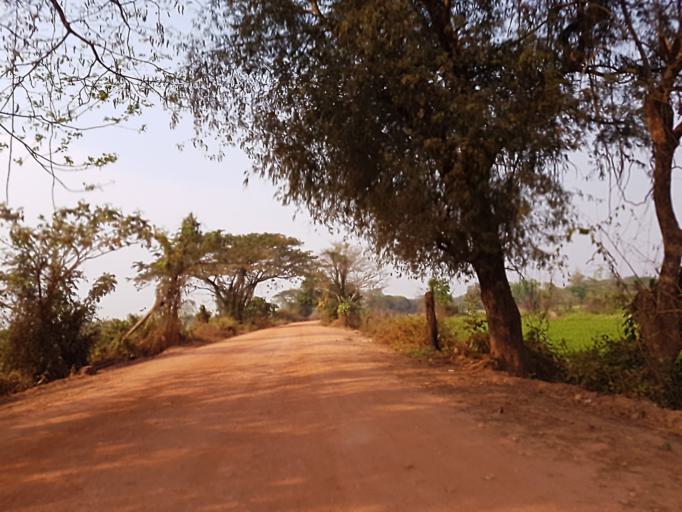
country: TH
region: Nong Khai
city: Phon Phisai
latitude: 18.0029
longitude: 102.9079
